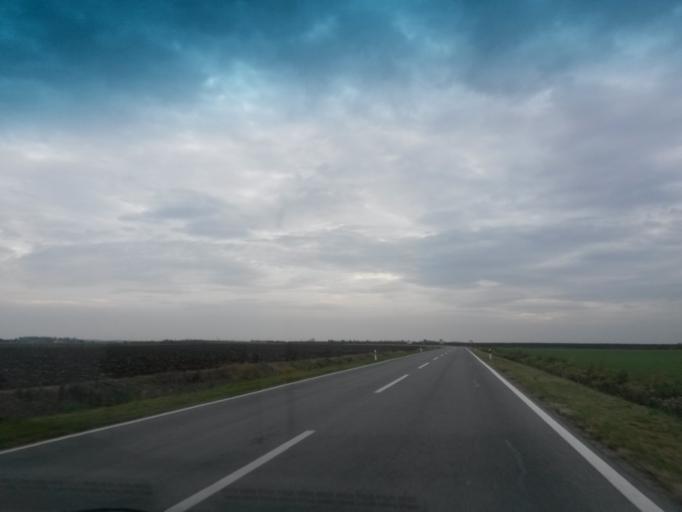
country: HR
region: Osjecko-Baranjska
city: Tenja
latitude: 45.5245
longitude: 18.7621
